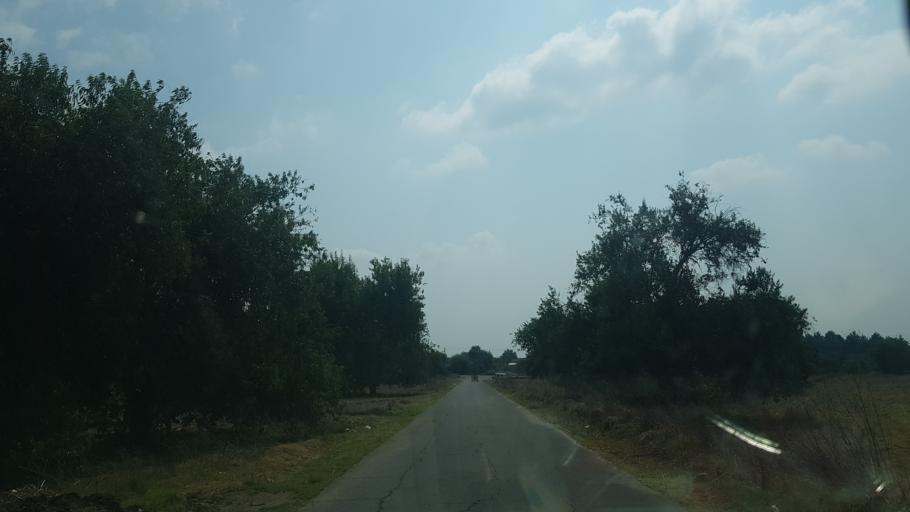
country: MX
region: Puebla
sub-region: Huejotzingo
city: San Juan Pancoac
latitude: 19.1288
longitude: -98.4216
